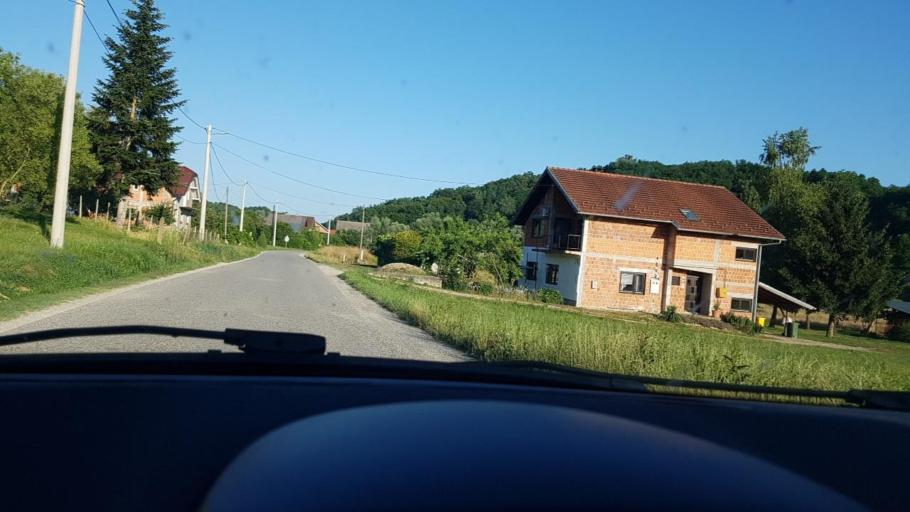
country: HR
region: Krapinsko-Zagorska
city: Bedekovcina
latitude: 46.0829
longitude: 15.9738
